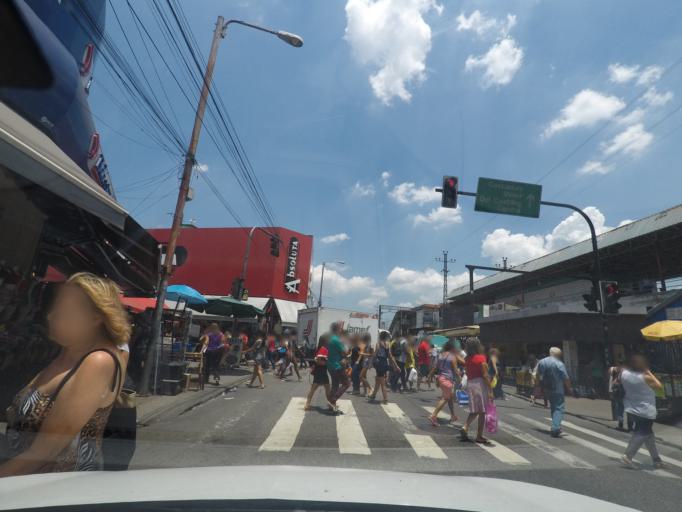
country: BR
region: Rio de Janeiro
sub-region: Sao Joao De Meriti
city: Sao Joao de Meriti
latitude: -22.8756
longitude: -43.3387
